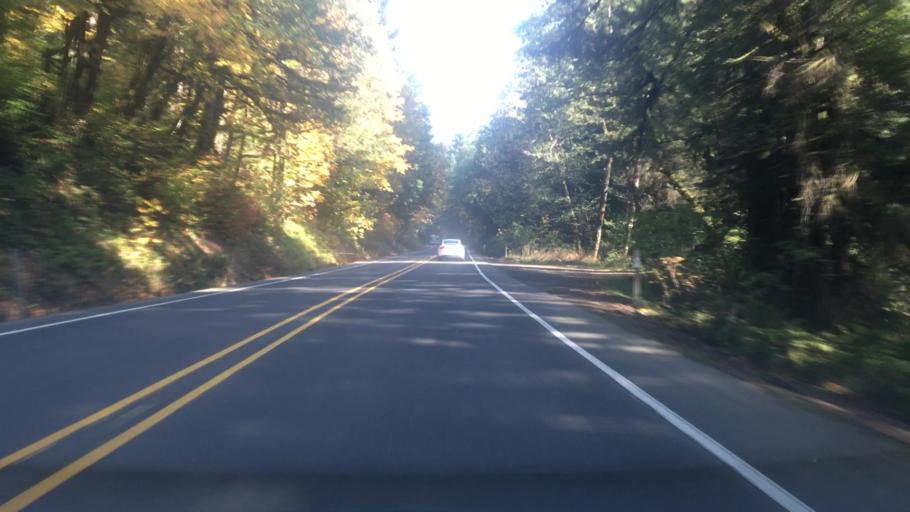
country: US
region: Oregon
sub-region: Lincoln County
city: Rose Lodge
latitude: 45.0524
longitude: -123.7760
